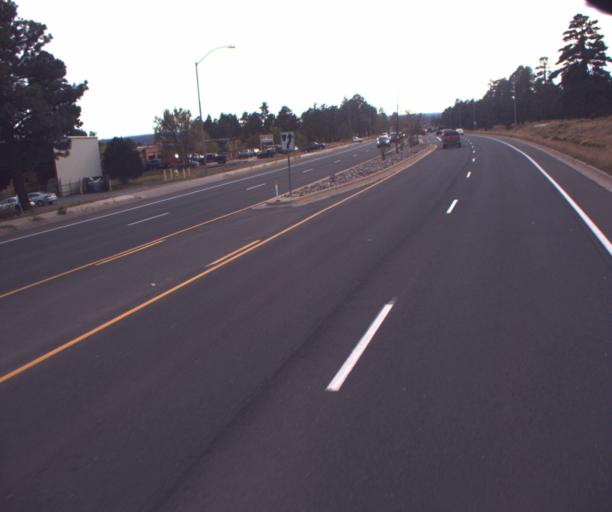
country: US
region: Arizona
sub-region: Coconino County
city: Flagstaff
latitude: 35.2382
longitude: -111.5725
